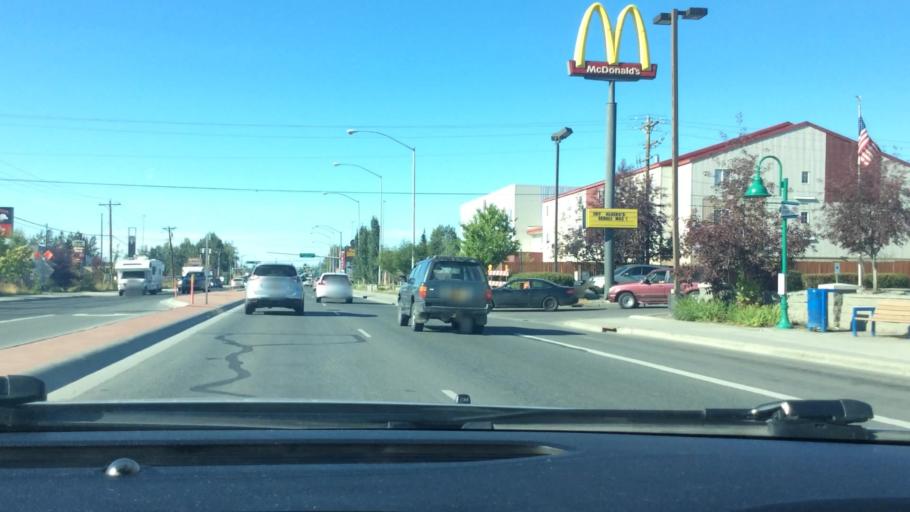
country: US
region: Alaska
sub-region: Anchorage Municipality
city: Elmendorf Air Force Base
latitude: 61.2209
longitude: -149.7334
